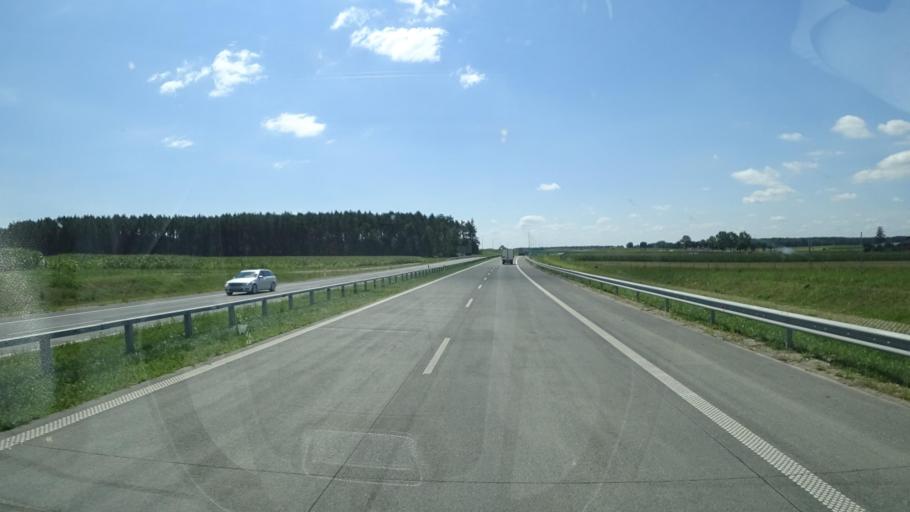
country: PL
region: Podlasie
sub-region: Powiat kolnenski
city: Stawiski
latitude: 53.4638
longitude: 22.2028
